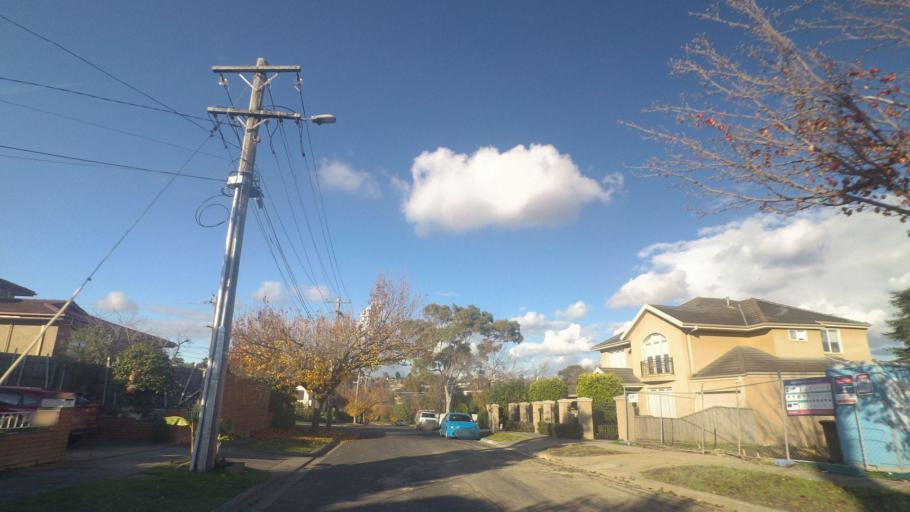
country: AU
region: Victoria
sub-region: Manningham
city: Templestowe Lower
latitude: -37.7785
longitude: 145.1058
